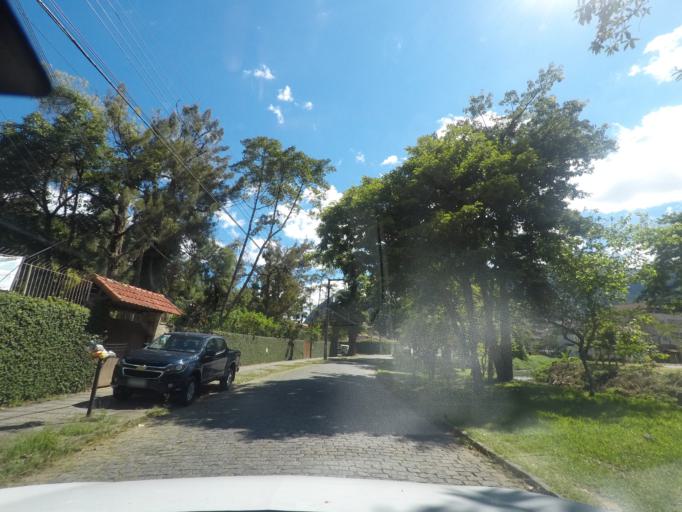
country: BR
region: Rio de Janeiro
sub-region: Teresopolis
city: Teresopolis
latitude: -22.4359
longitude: -42.9748
